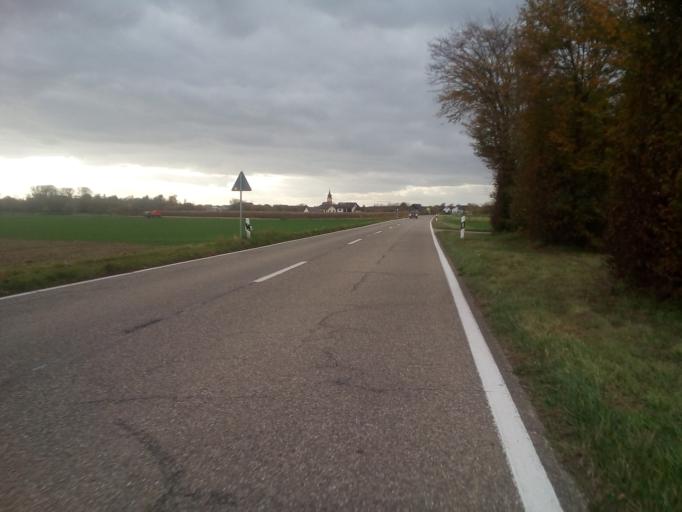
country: DE
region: Baden-Wuerttemberg
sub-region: Karlsruhe Region
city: Schwarzach
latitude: 48.7638
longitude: 8.0624
